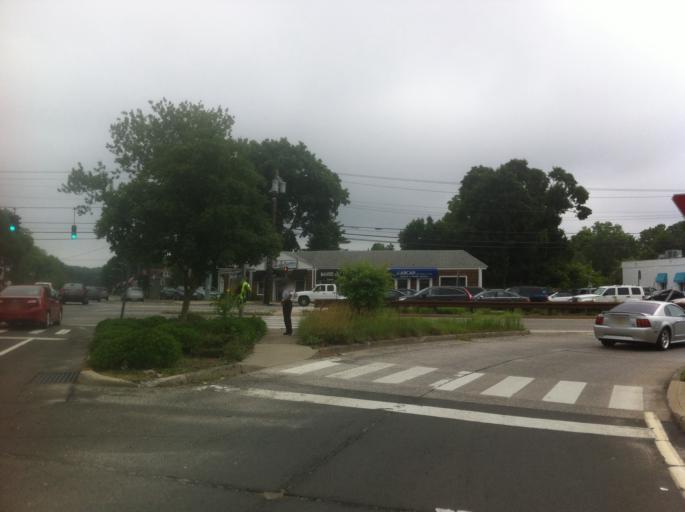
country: US
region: New York
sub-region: Nassau County
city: East Norwich
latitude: 40.8426
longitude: -73.5332
